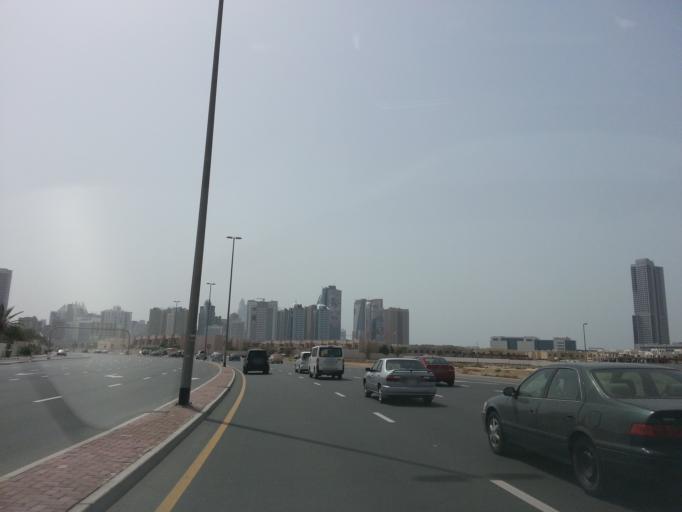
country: AE
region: Dubai
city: Dubai
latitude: 25.1057
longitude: 55.1902
